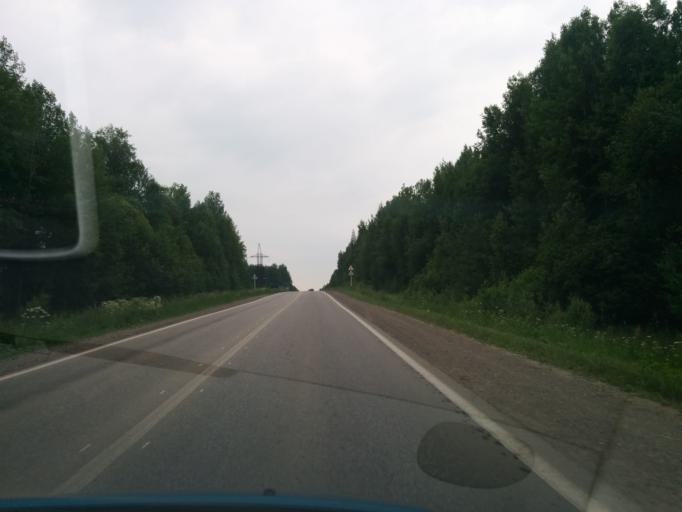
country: RU
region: Perm
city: Perm
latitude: 58.1433
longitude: 56.2654
